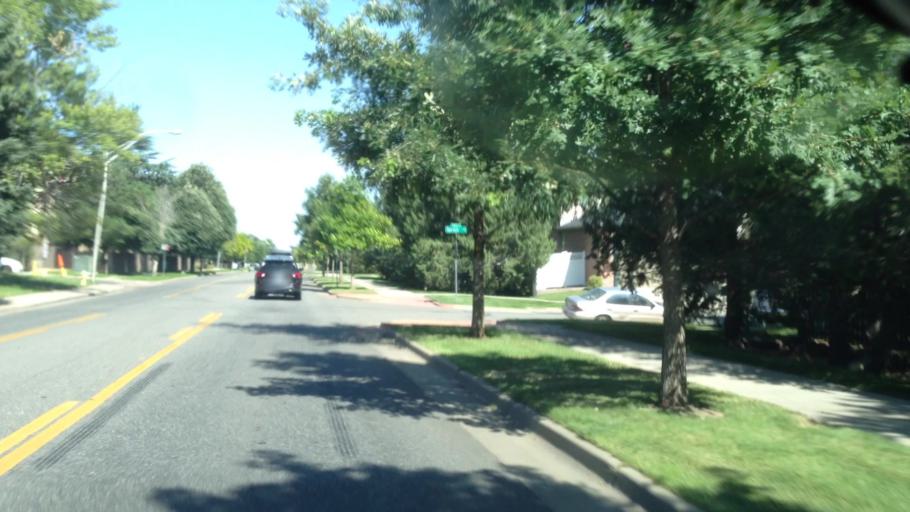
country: US
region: Colorado
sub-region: Arapahoe County
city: Glendale
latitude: 39.7328
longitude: -104.8973
